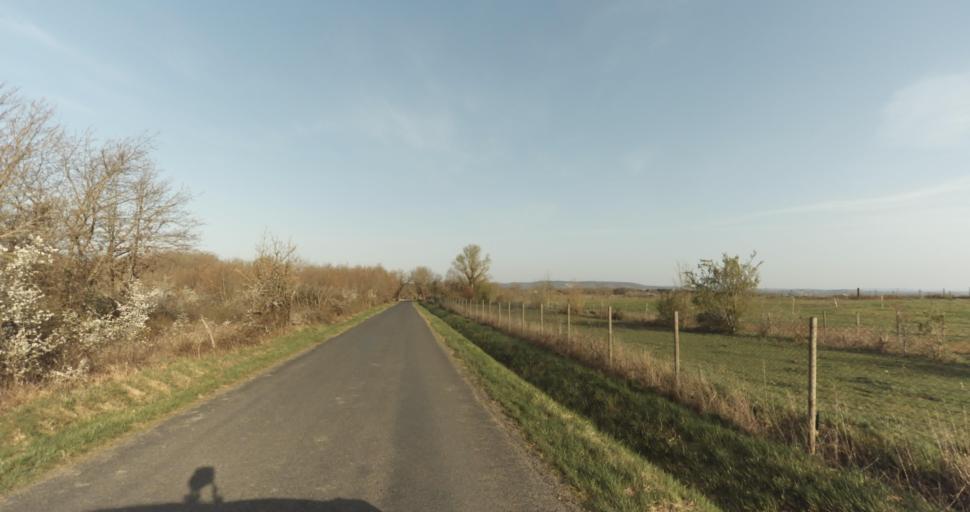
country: FR
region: Midi-Pyrenees
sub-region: Departement du Tarn
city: Saint-Sulpice-la-Pointe
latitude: 43.7354
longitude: 1.6920
